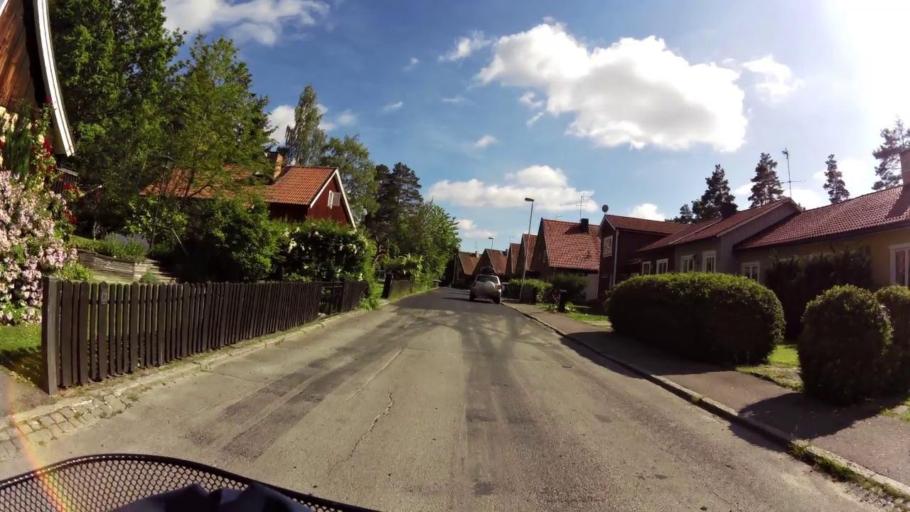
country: SE
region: OEstergoetland
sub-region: Linkopings Kommun
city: Linkoping
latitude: 58.3918
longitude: 15.6582
